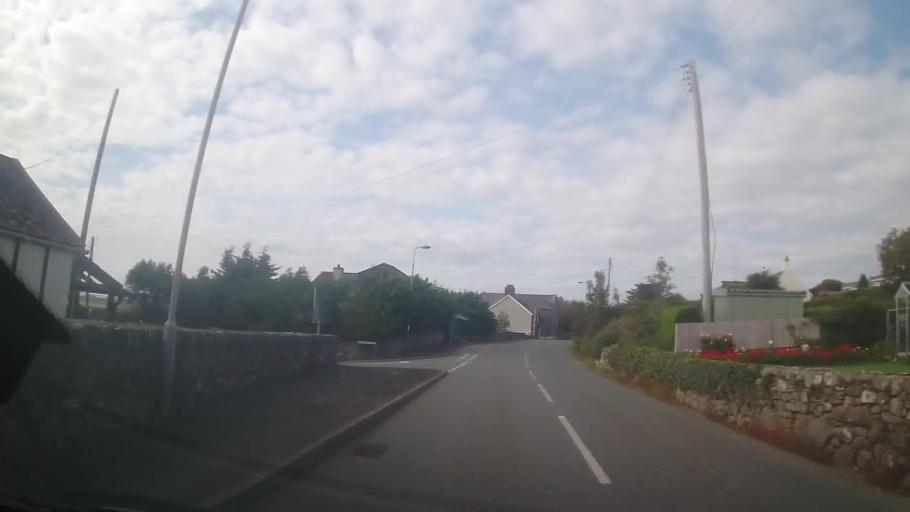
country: GB
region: Wales
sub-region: Gwynedd
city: Llanbedr
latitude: 52.7935
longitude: -4.0996
